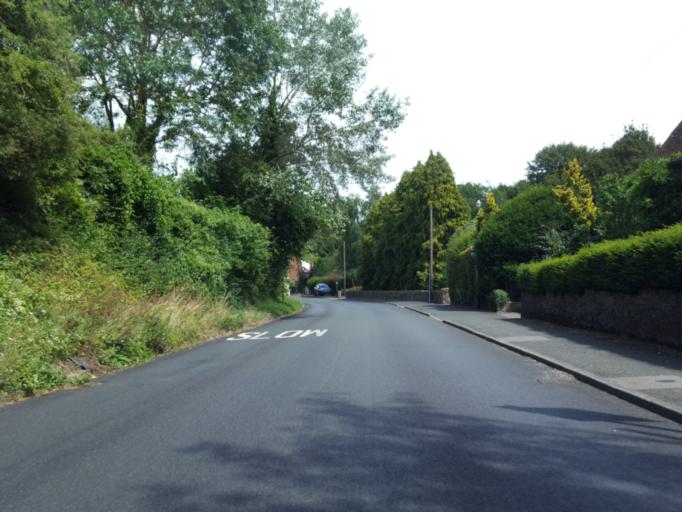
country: GB
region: England
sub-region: Kent
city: West Malling
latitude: 51.2865
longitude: 0.4017
